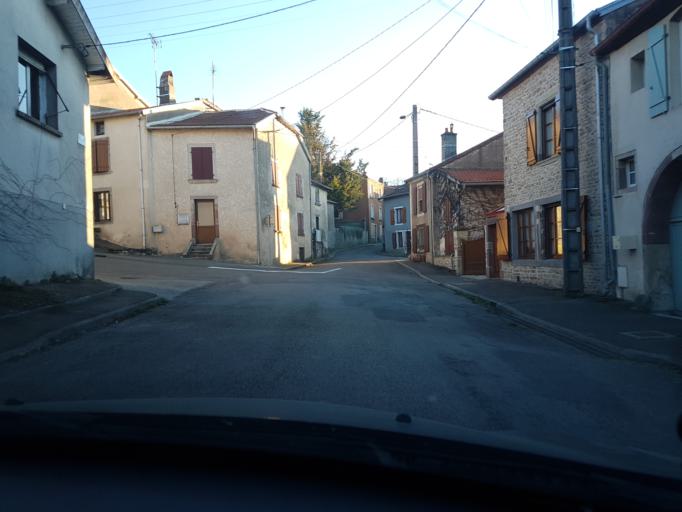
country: FR
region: Franche-Comte
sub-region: Departement de la Haute-Saone
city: Faverney
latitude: 47.9214
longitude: 6.0965
